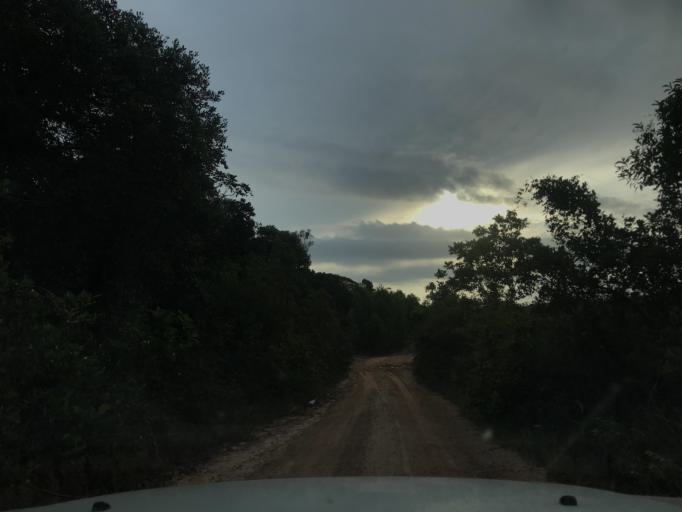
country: BR
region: Bahia
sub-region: Entre Rios
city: Entre Rios
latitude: -12.0531
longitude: -38.2235
